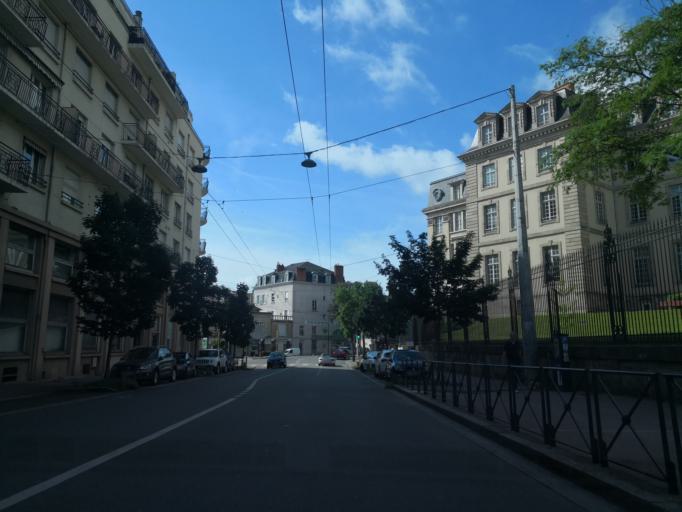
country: FR
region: Limousin
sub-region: Departement de la Haute-Vienne
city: Limoges
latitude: 45.8309
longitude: 1.2627
